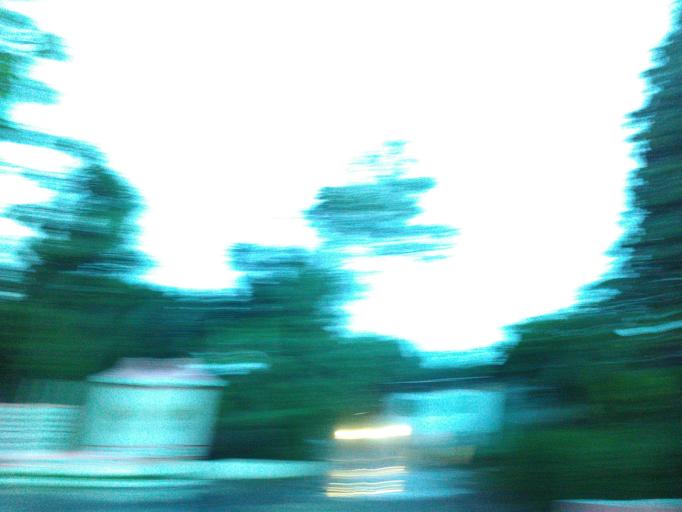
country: ID
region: Central Java
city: Ceper
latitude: -7.6536
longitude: 110.6724
